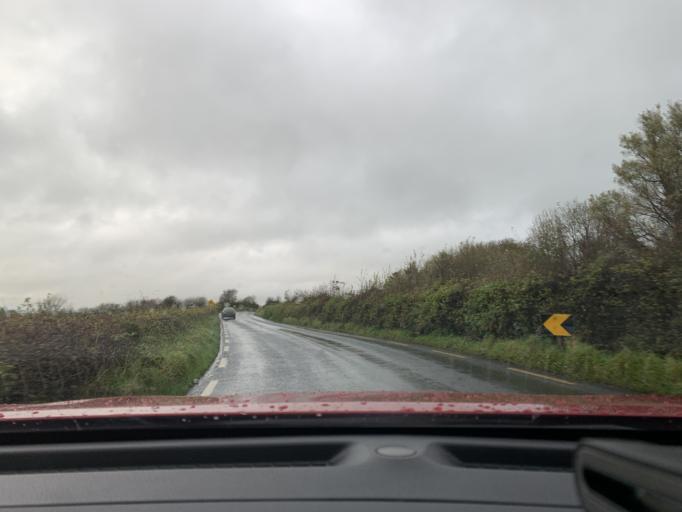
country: IE
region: Connaught
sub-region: Sligo
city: Ballymote
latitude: 54.0622
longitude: -8.5076
